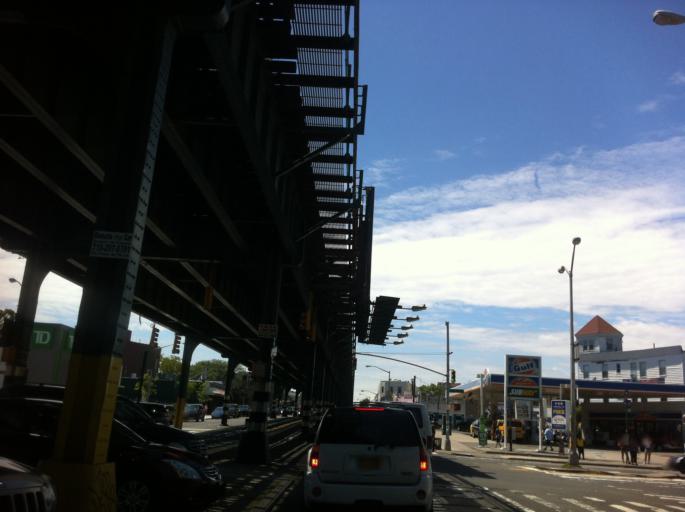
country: US
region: New York
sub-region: Bronx
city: The Bronx
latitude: 40.8333
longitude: -73.8617
